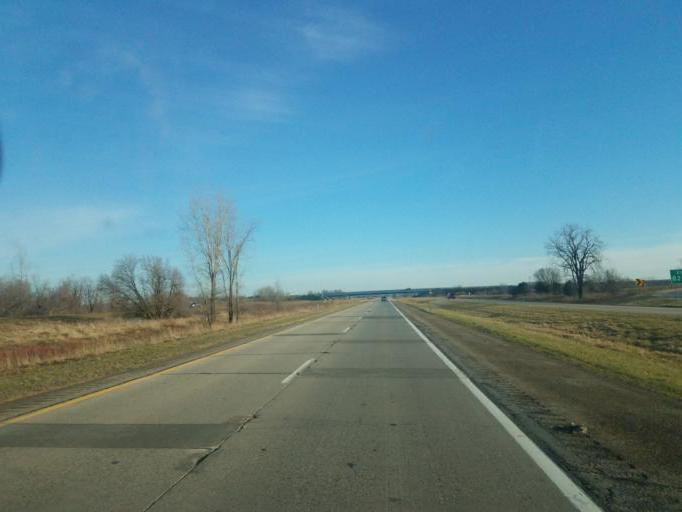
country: US
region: Michigan
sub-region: Clinton County
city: Bath
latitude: 42.8003
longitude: -84.5117
